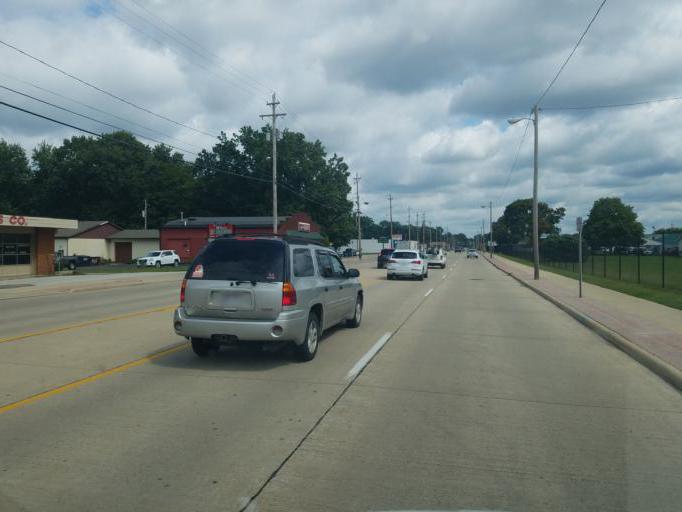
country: US
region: Ohio
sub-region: Lake County
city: Painesville
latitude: 41.7026
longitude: -81.2733
